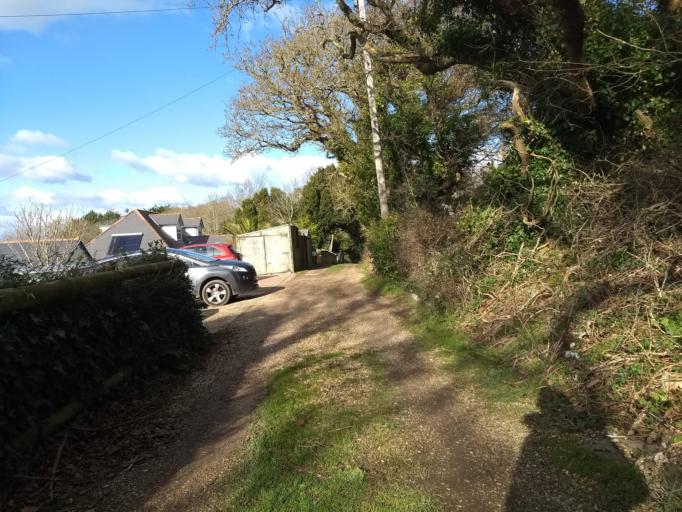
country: GB
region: England
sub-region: Isle of Wight
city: Bembridge
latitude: 50.6764
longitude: -1.0940
